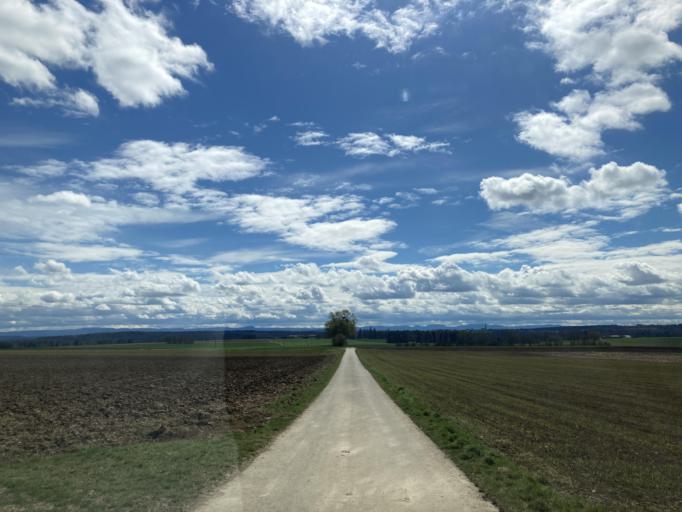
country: DE
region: Baden-Wuerttemberg
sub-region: Regierungsbezirk Stuttgart
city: Bondorf
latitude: 48.4668
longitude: 8.8158
